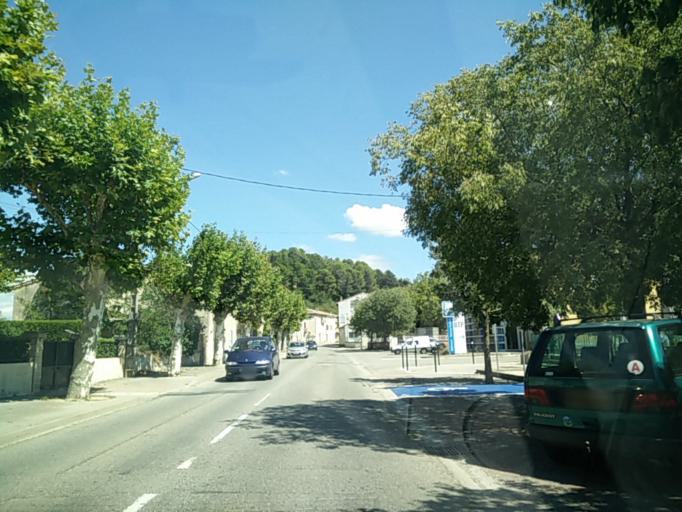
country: FR
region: Rhone-Alpes
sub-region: Departement de la Drome
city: Montboucher-sur-Jabron
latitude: 44.5544
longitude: 4.8620
